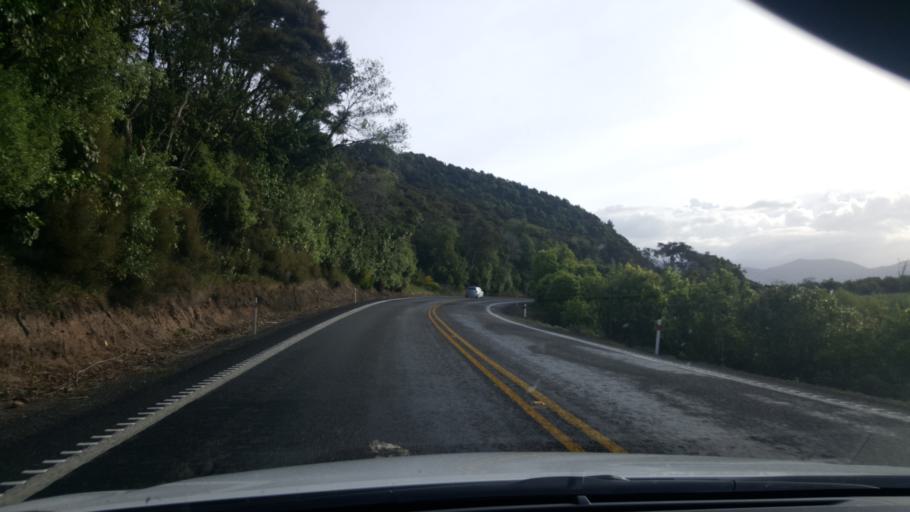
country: NZ
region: Waikato
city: Turangi
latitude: -38.9404
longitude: 175.8584
